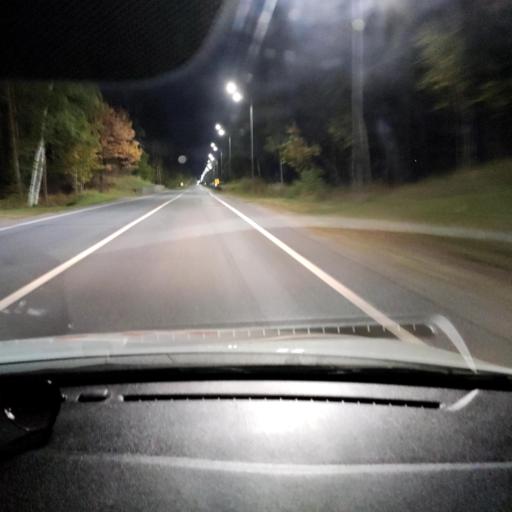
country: RU
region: Tatarstan
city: Verkhniy Uslon
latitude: 55.6367
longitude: 49.0594
